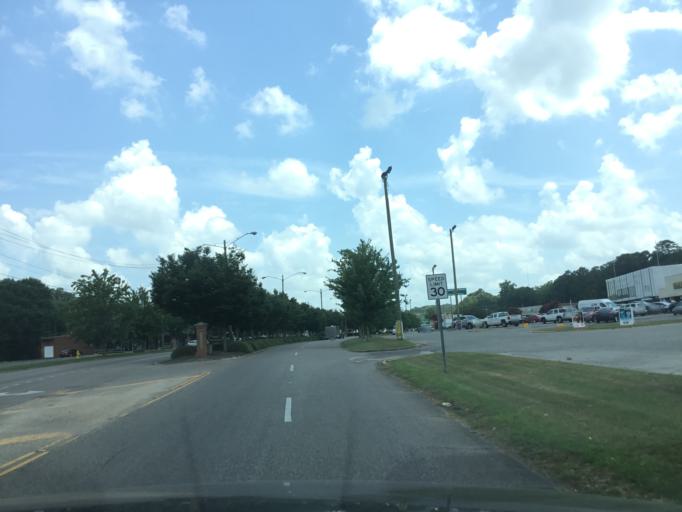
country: US
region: Alabama
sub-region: Montgomery County
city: Montgomery
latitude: 32.3927
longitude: -86.2578
